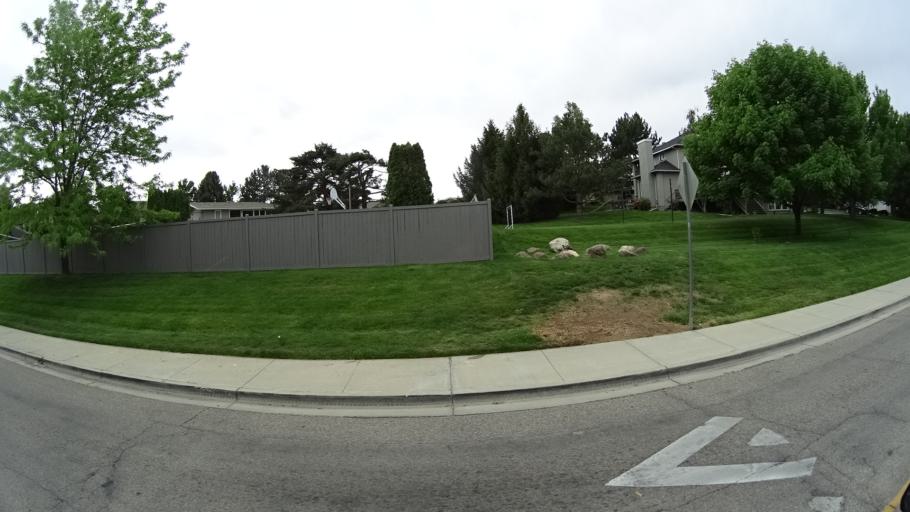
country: US
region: Idaho
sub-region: Ada County
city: Boise
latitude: 43.6173
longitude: -116.1697
